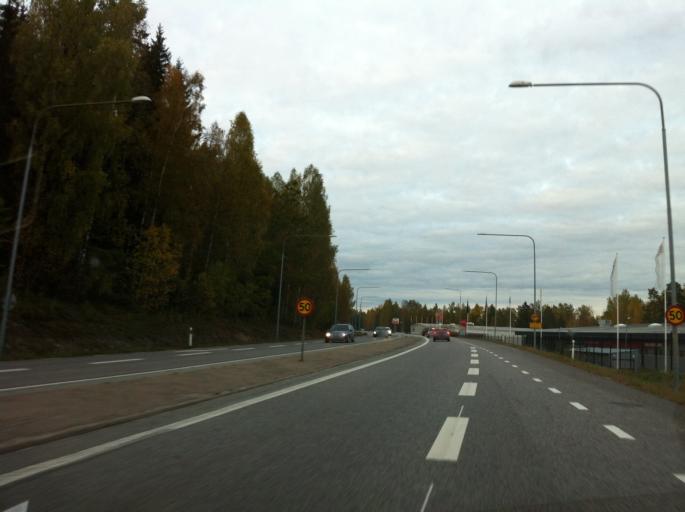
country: SE
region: OErebro
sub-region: Nora Kommun
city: Nora
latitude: 59.4933
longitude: 15.0520
